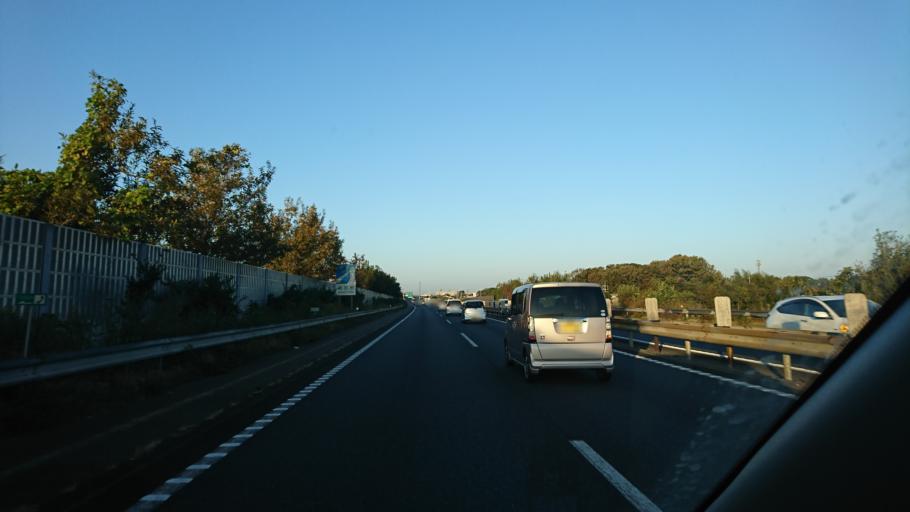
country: JP
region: Hyogo
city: Kakogawacho-honmachi
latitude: 34.7164
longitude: 134.9135
